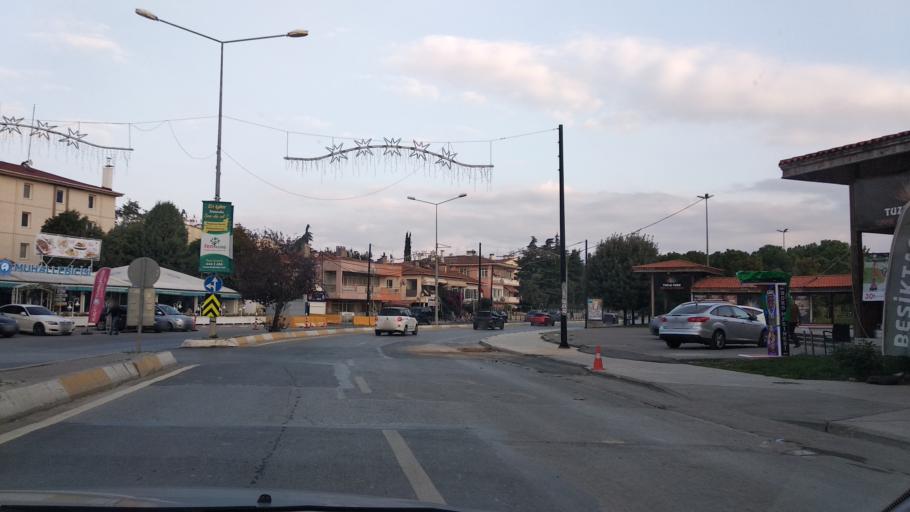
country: TR
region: Istanbul
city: Icmeler
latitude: 40.8148
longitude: 29.3059
